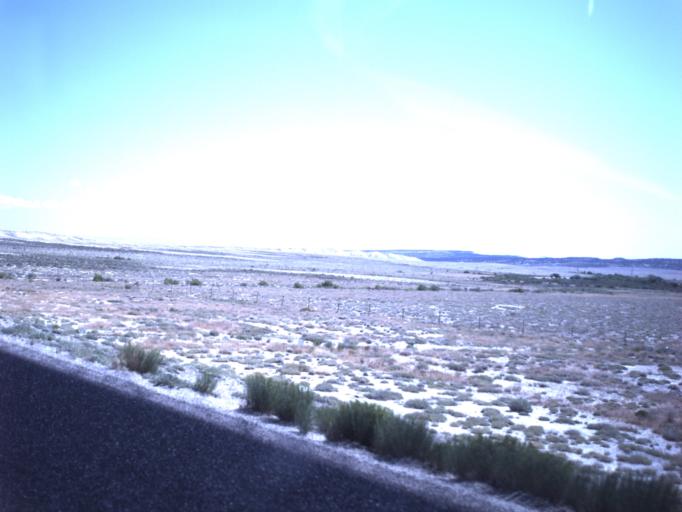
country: US
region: Utah
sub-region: Emery County
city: Ferron
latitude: 38.9741
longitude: -111.1784
